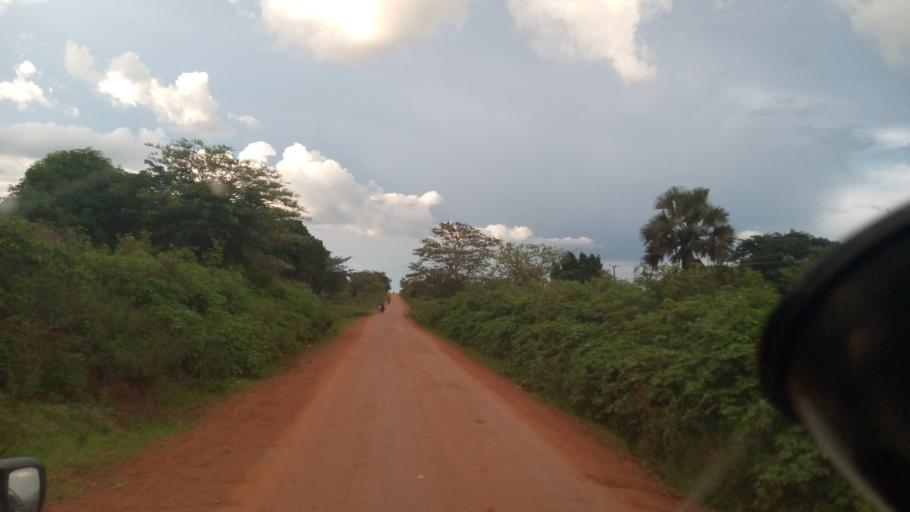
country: UG
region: Northern Region
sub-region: Kole District
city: Kole
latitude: 2.3855
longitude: 32.9328
